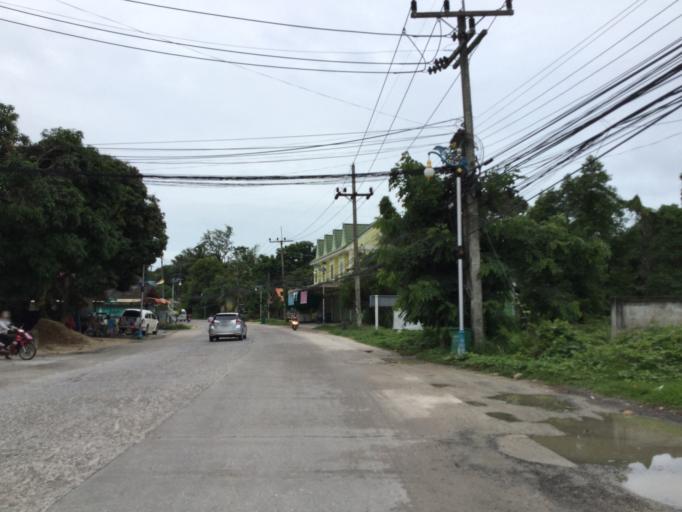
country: TH
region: Surat Thani
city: Ko Pha-Ngan
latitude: 9.7137
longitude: 99.9926
